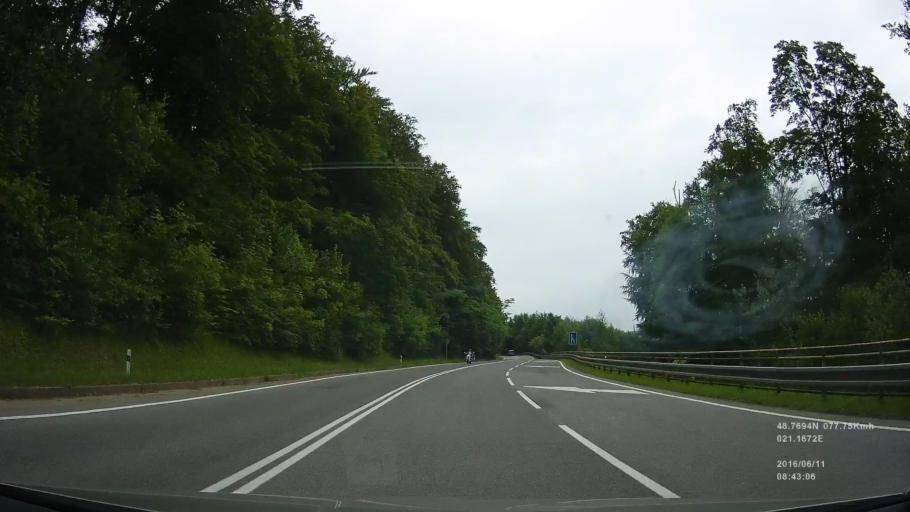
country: SK
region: Kosicky
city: Kosice
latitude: 48.7656
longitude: 21.1660
